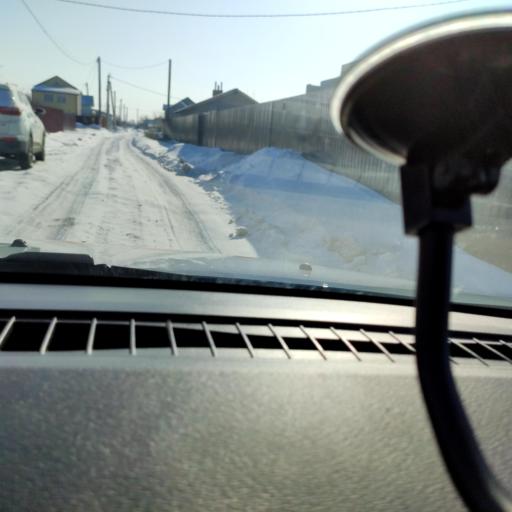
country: RU
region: Samara
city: Samara
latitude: 53.1370
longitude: 50.2506
